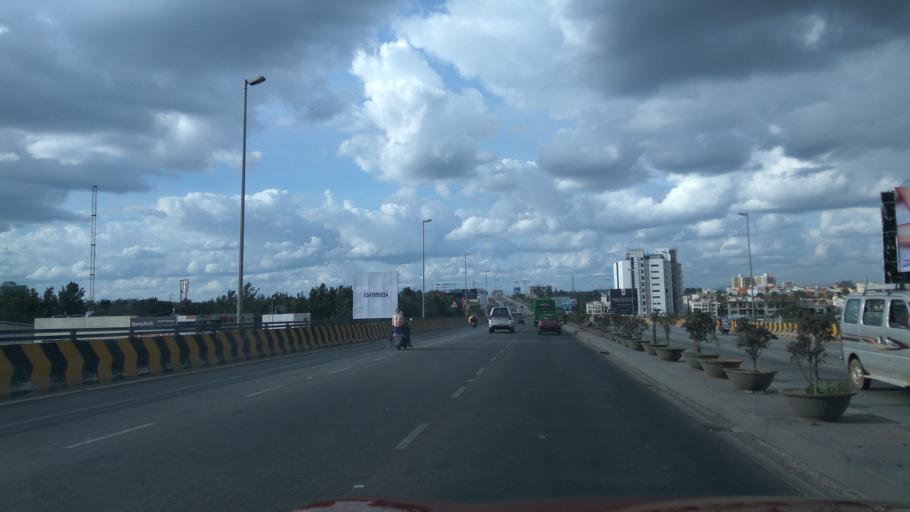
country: IN
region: Karnataka
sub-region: Bangalore Urban
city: Yelahanka
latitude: 13.0585
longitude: 77.5934
